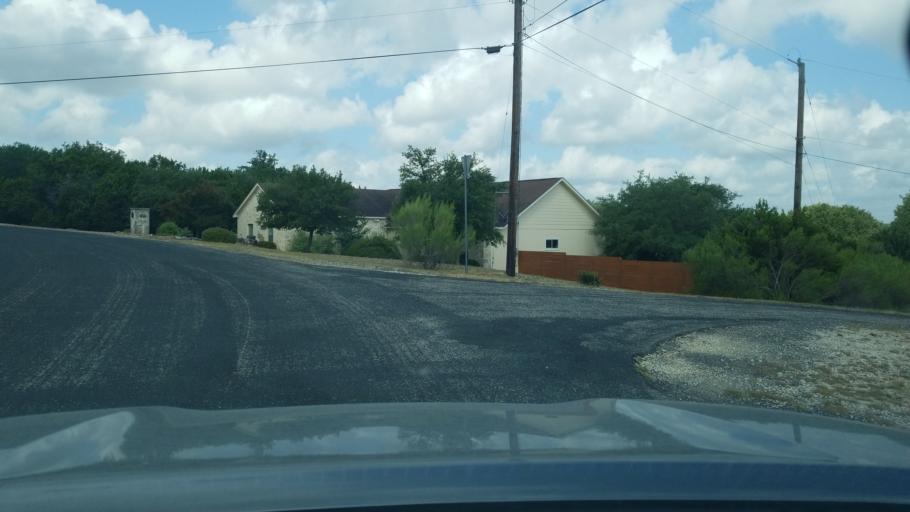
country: US
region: Texas
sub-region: Bexar County
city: Timberwood Park
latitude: 29.6895
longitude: -98.5128
